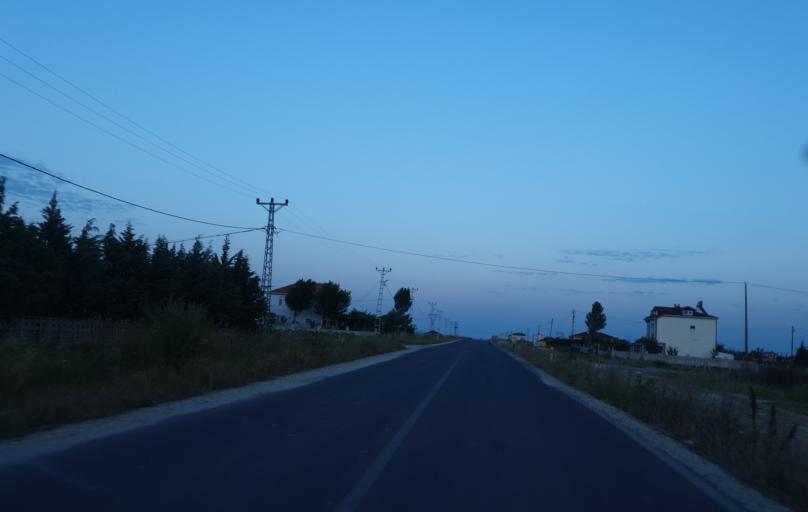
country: TR
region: Tekirdag
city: Velimese
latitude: 41.3424
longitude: 27.8993
